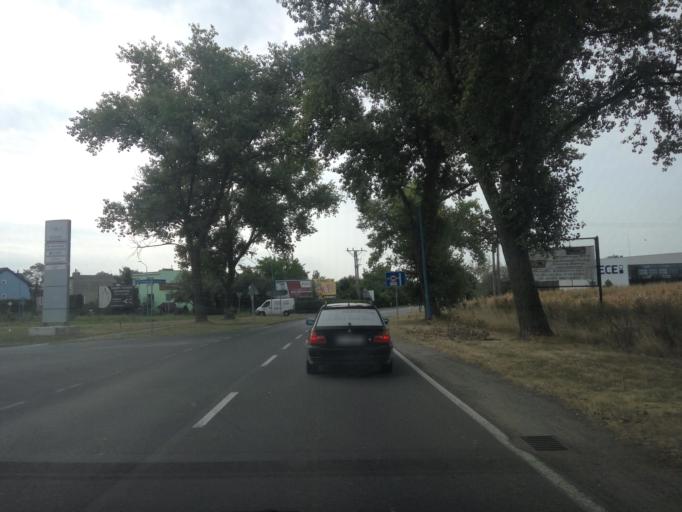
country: PL
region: Lower Silesian Voivodeship
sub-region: Powiat strzelinski
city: Strzelin
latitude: 50.7939
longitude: 17.0657
